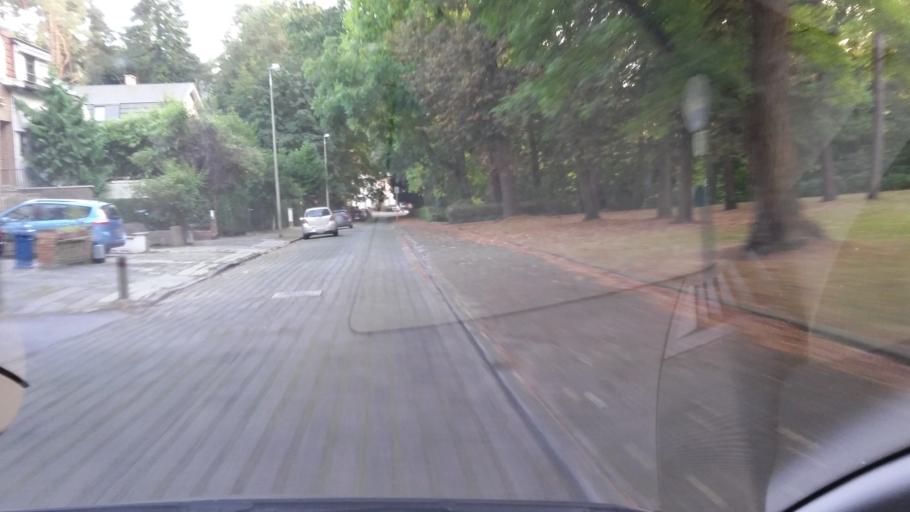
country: BE
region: Flanders
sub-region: Provincie Vlaams-Brabant
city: Hoeilaart
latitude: 50.8056
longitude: 4.4292
